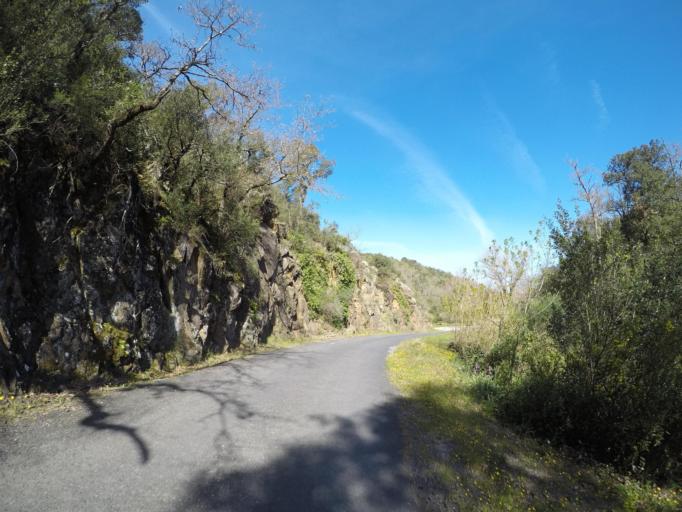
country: FR
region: Languedoc-Roussillon
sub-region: Departement des Pyrenees-Orientales
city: Thuir
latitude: 42.6247
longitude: 2.7046
